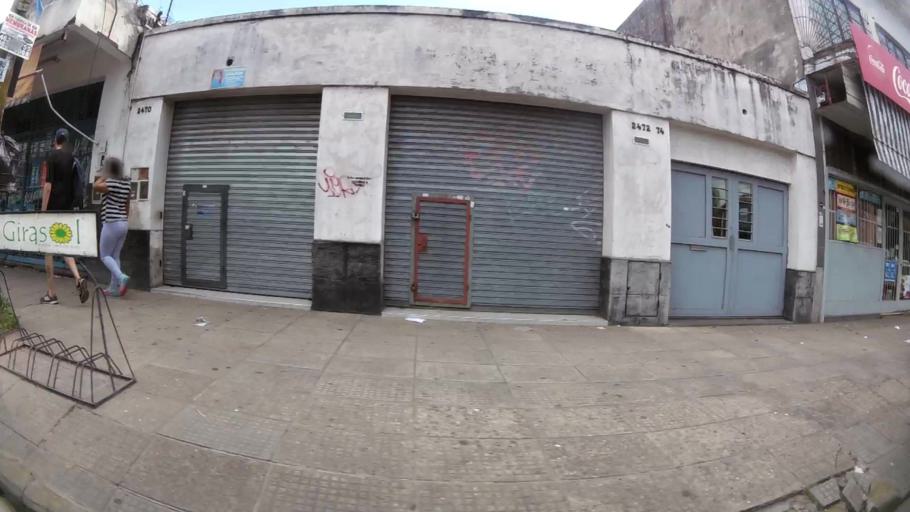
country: AR
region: Buenos Aires
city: Ituzaingo
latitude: -34.6401
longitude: -58.6891
